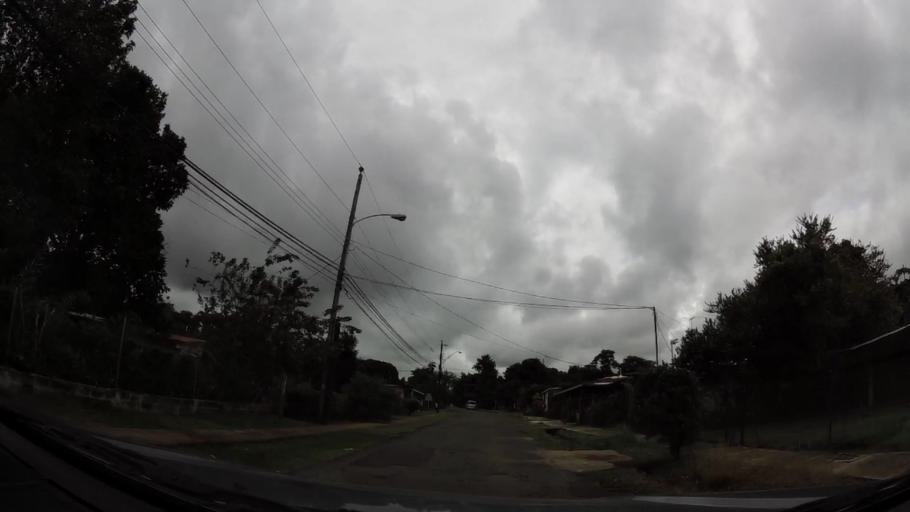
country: PA
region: Chiriqui
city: Dolega District
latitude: 8.5651
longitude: -82.4127
